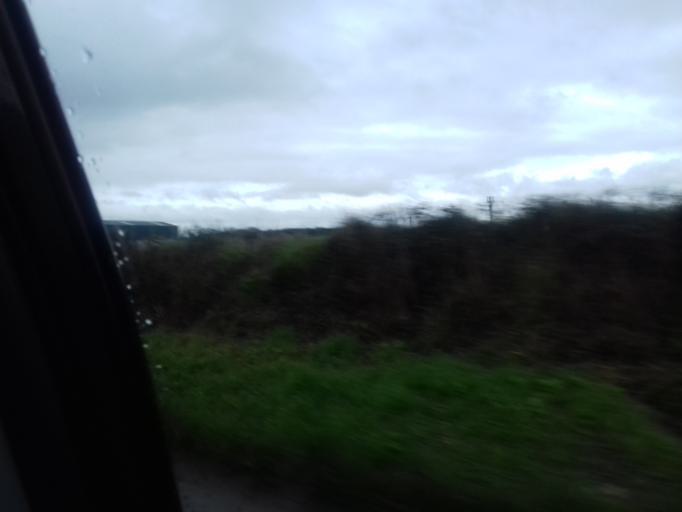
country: IE
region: Leinster
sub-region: County Carlow
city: Bagenalstown
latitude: 52.6254
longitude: -6.9915
